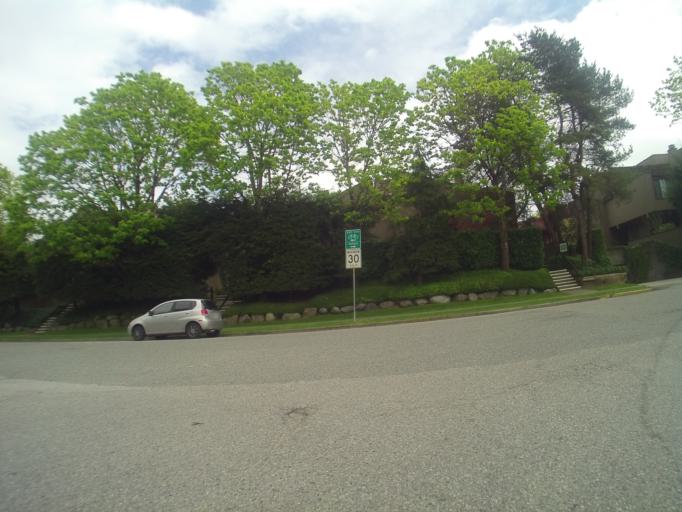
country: CA
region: British Columbia
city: Vancouver
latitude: 49.2469
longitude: -123.1549
